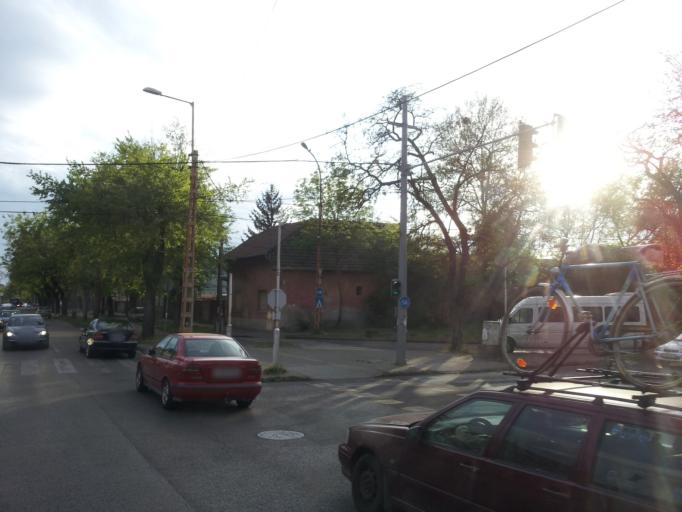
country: HU
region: Budapest
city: Budapest XV. keruelet
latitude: 47.5663
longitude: 19.1229
